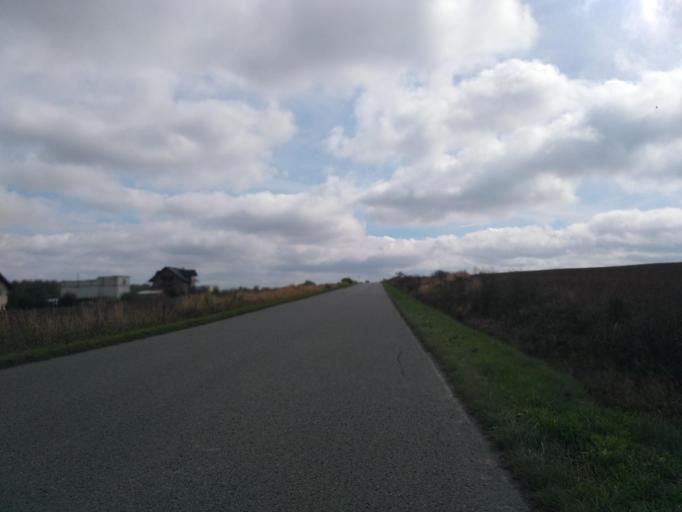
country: PL
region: Subcarpathian Voivodeship
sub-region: Powiat ropczycko-sedziszowski
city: Niedzwiada
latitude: 49.9394
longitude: 21.5060
